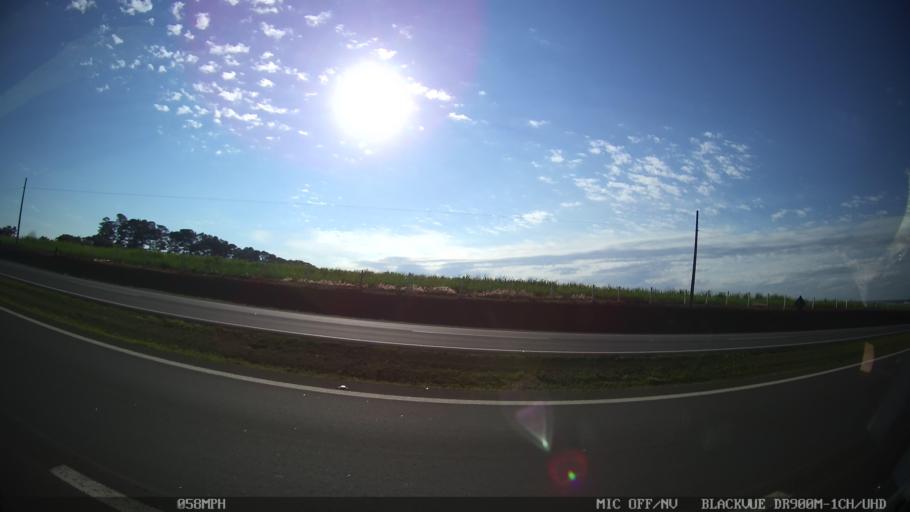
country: BR
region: Sao Paulo
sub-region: Piracicaba
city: Piracicaba
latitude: -22.6897
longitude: -47.6433
